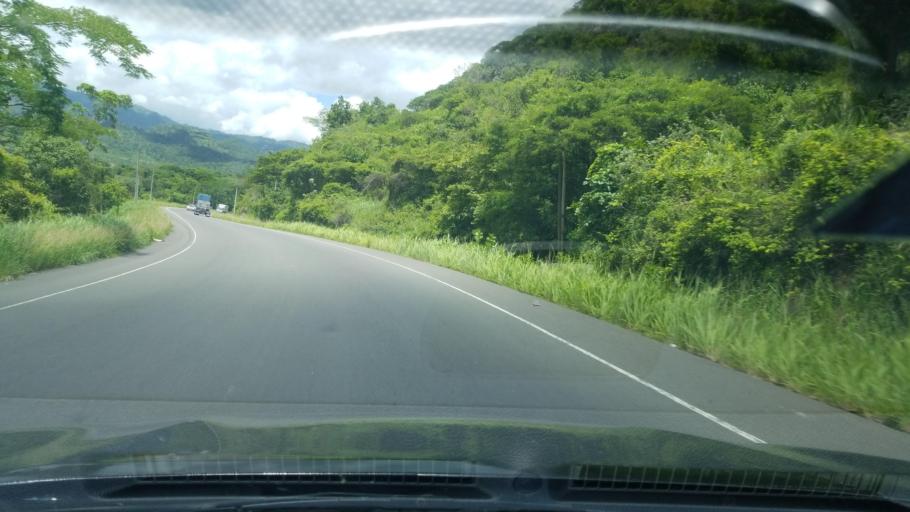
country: HN
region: Francisco Morazan
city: Rio Abajo
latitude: 14.1940
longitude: -87.2061
